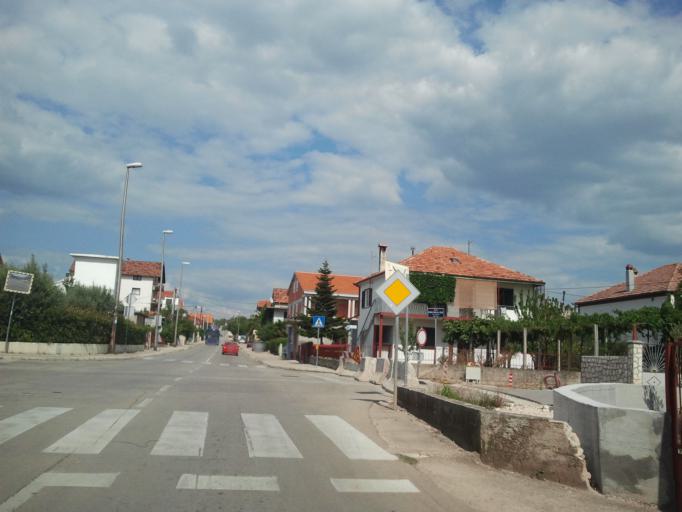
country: HR
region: Zadarska
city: Zadar
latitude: 44.1210
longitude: 15.2500
